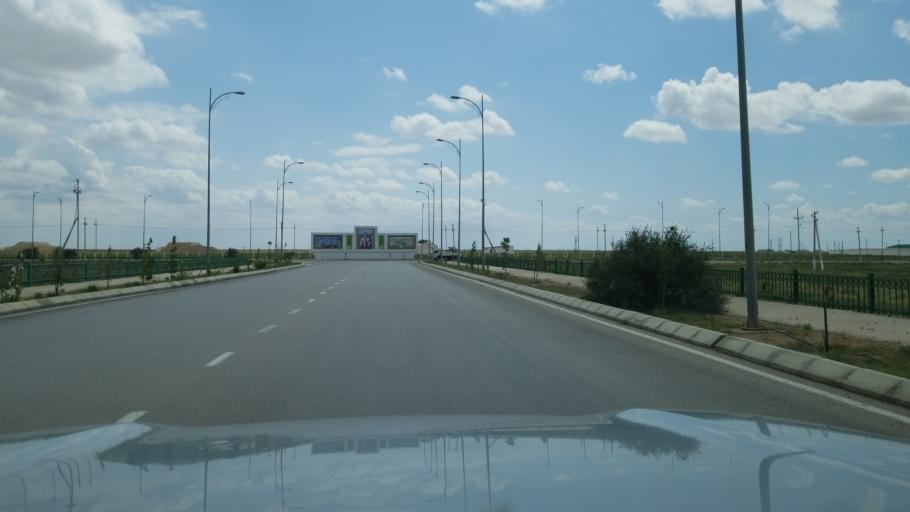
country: TM
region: Balkan
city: Balkanabat
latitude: 39.4875
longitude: 54.3749
